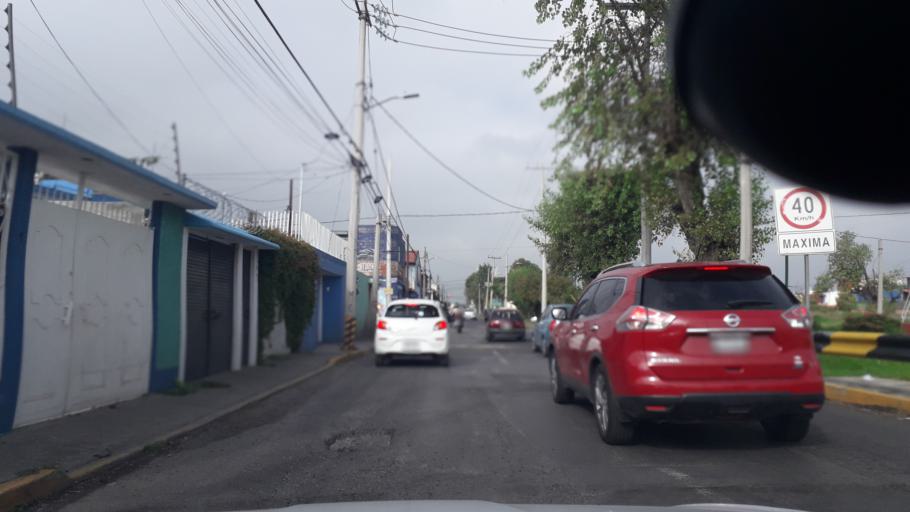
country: MX
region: Mexico
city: Coacalco
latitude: 19.6449
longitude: -99.0996
